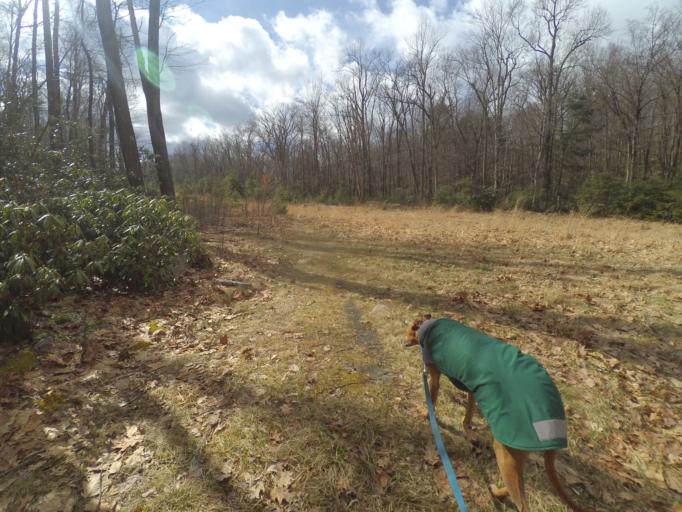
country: US
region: Pennsylvania
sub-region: Centre County
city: Boalsburg
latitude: 40.7451
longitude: -77.7205
